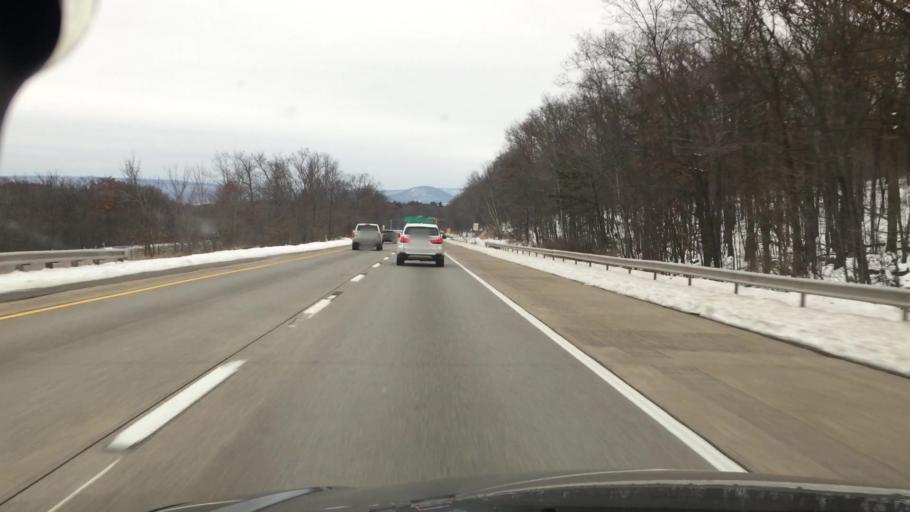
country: US
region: Pennsylvania
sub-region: Luzerne County
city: Conyngham
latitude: 41.0533
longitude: -76.0056
